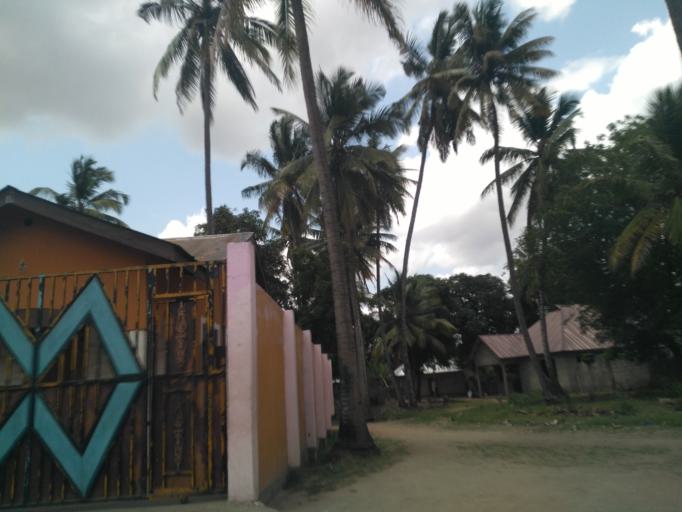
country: TZ
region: Dar es Salaam
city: Dar es Salaam
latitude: -6.8627
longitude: 39.3533
